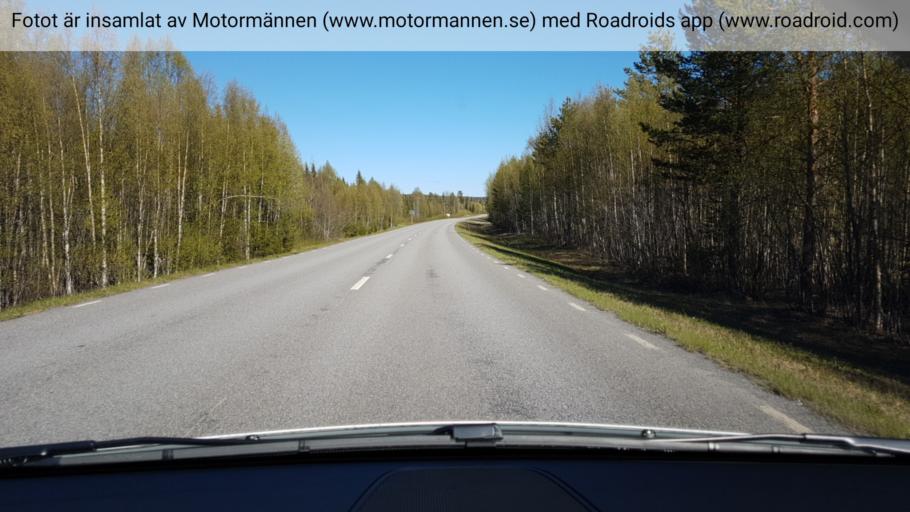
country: SE
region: Jaemtland
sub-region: Stroemsunds Kommun
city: Stroemsund
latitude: 64.3074
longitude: 15.2516
